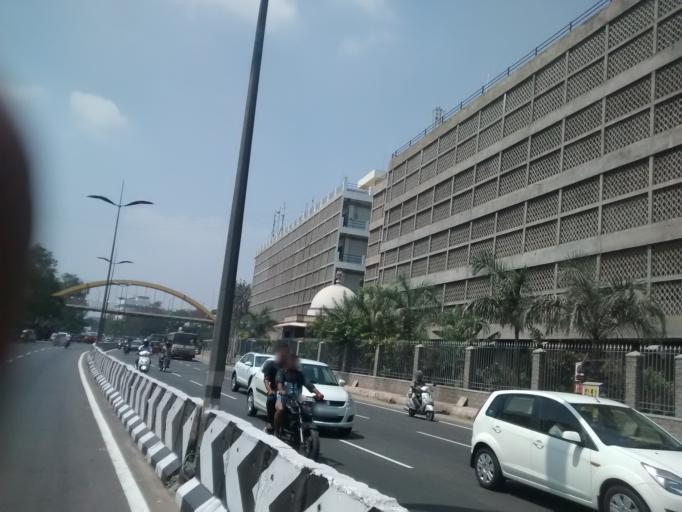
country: IN
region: Tamil Nadu
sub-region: Coimbatore
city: Singanallur
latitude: 11.0240
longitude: 77.0048
